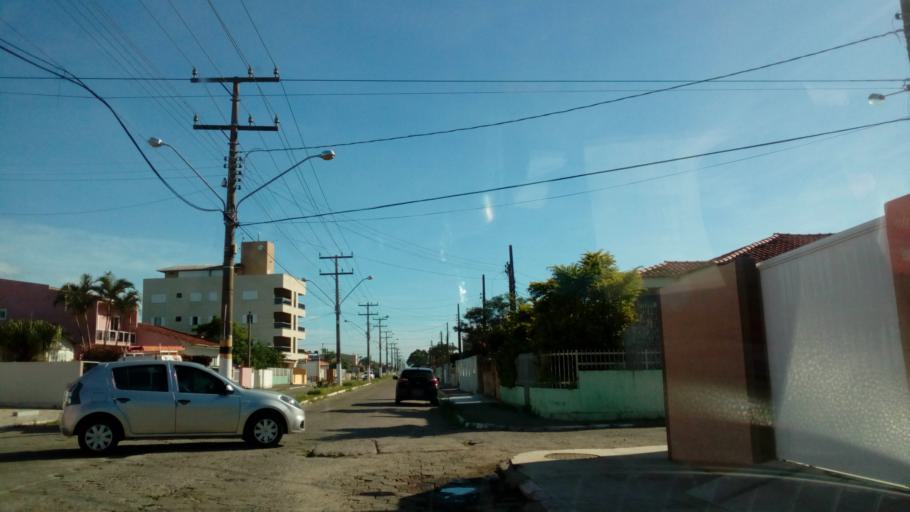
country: BR
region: Santa Catarina
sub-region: Laguna
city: Laguna
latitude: -28.4787
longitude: -48.7835
